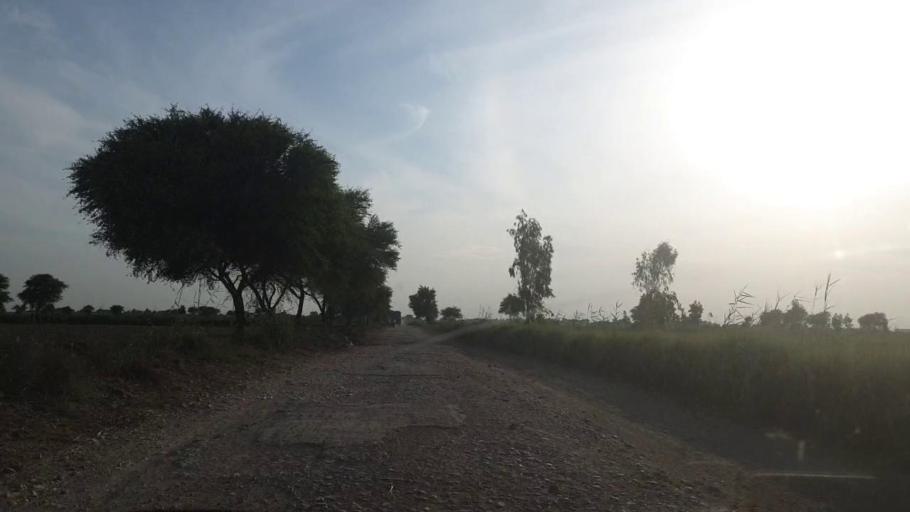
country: PK
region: Sindh
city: Tando Muhammad Khan
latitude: 25.2072
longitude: 68.5026
